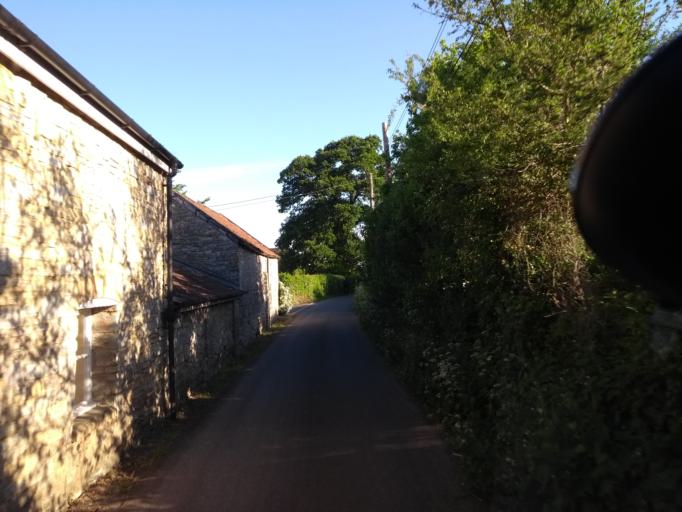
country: GB
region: England
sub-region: Somerset
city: Creech Saint Michael
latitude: 51.0002
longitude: -3.0523
